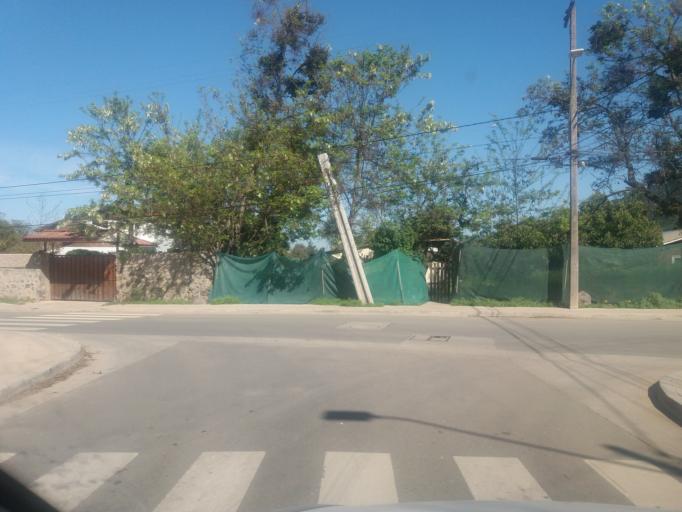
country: CL
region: Valparaiso
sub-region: Provincia de Marga Marga
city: Limache
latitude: -32.9900
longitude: -71.1636
